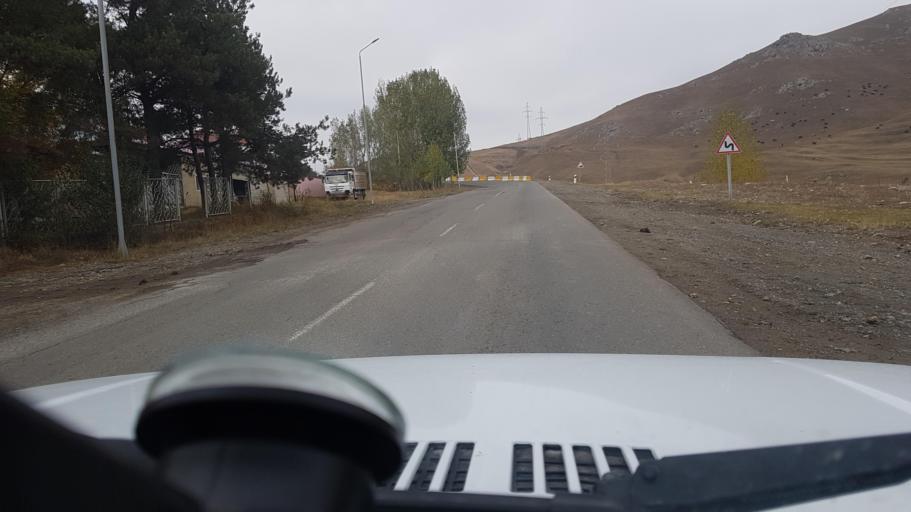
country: AZ
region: Gadabay Rayon
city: Ariqdam
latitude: 40.6110
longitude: 45.8128
